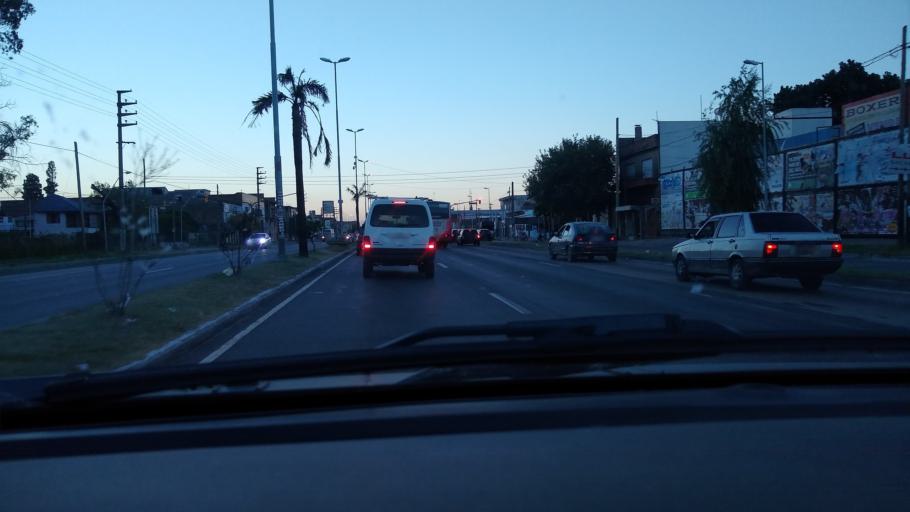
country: AR
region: Buenos Aires
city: San Justo
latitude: -34.6925
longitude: -58.5513
